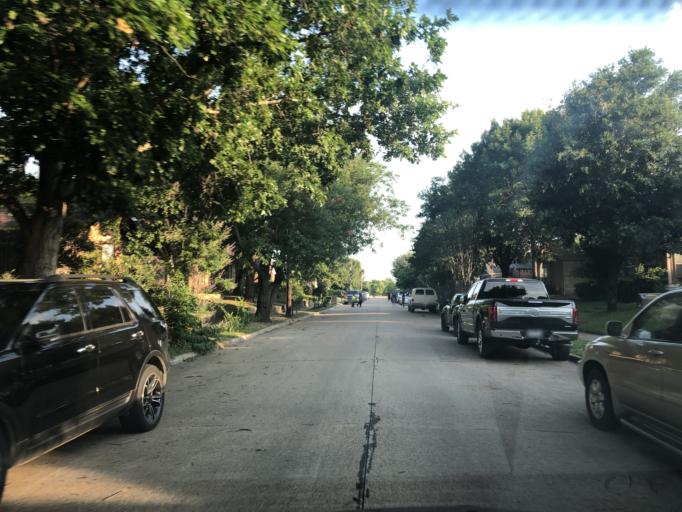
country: US
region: Texas
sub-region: Dallas County
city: Irving
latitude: 32.7849
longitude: -96.9615
